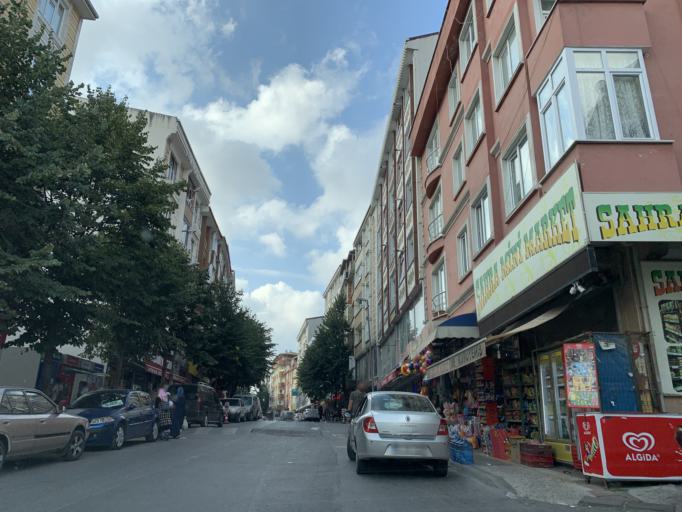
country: TR
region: Istanbul
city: Esenyurt
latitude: 41.0257
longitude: 28.6753
